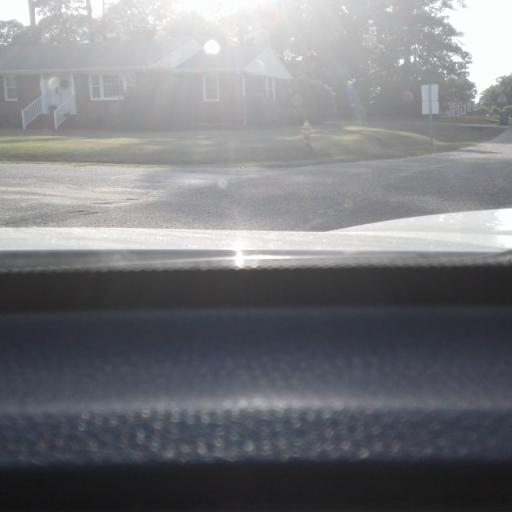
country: US
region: North Carolina
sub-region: Harnett County
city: Dunn
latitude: 35.3156
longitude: -78.6186
